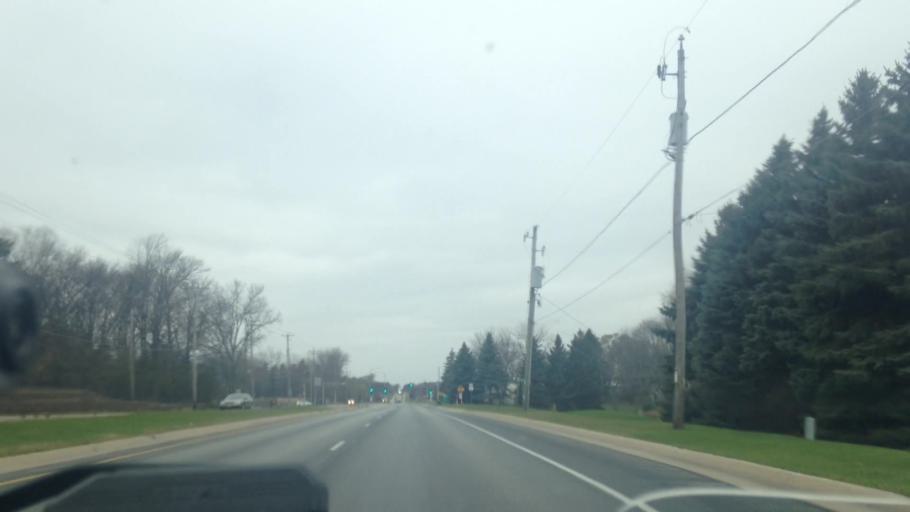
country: US
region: Wisconsin
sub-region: Waukesha County
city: Lannon
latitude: 43.1932
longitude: -88.1793
